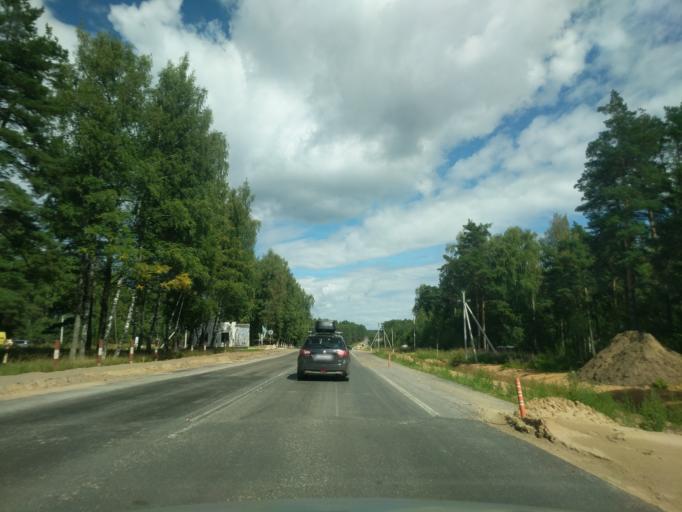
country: RU
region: Jaroslavl
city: Levashevo
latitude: 57.6693
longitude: 40.5787
